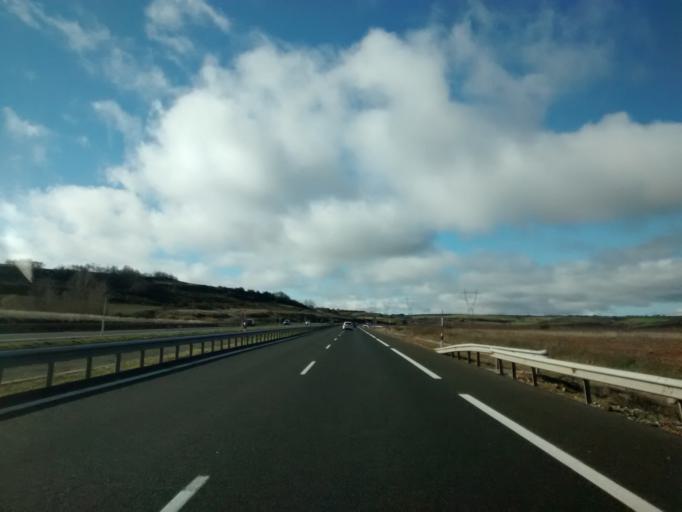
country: ES
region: Cantabria
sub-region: Provincia de Cantabria
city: Mataporquera
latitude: 42.8437
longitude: -4.1775
